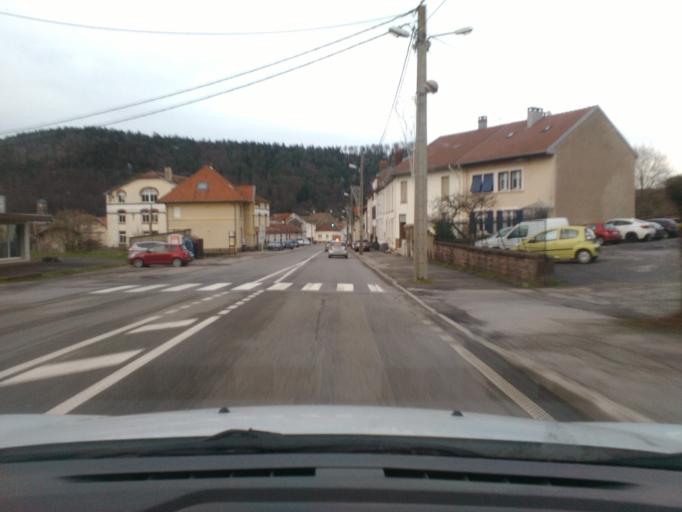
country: FR
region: Lorraine
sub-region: Departement des Vosges
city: Etival-Clairefontaine
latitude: 48.4025
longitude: 6.8470
